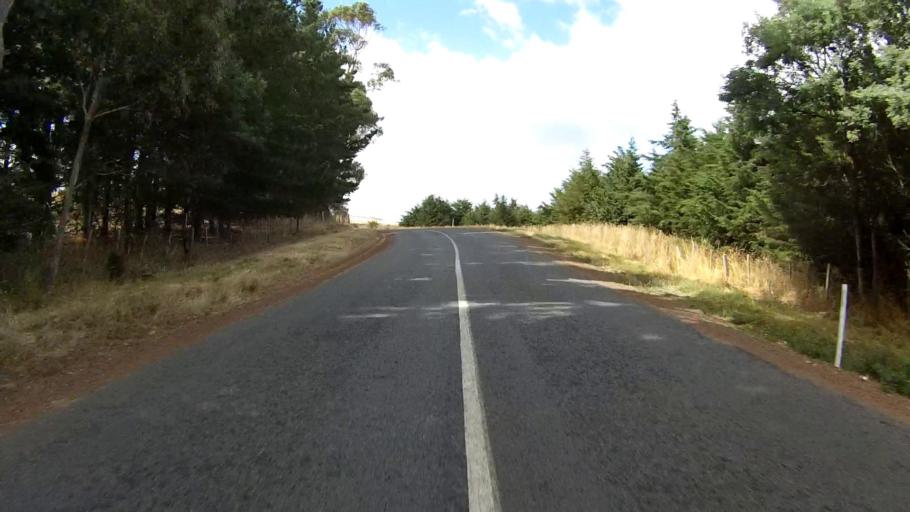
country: AU
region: Tasmania
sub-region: Northern Midlands
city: Evandale
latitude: -41.6959
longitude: 147.3671
